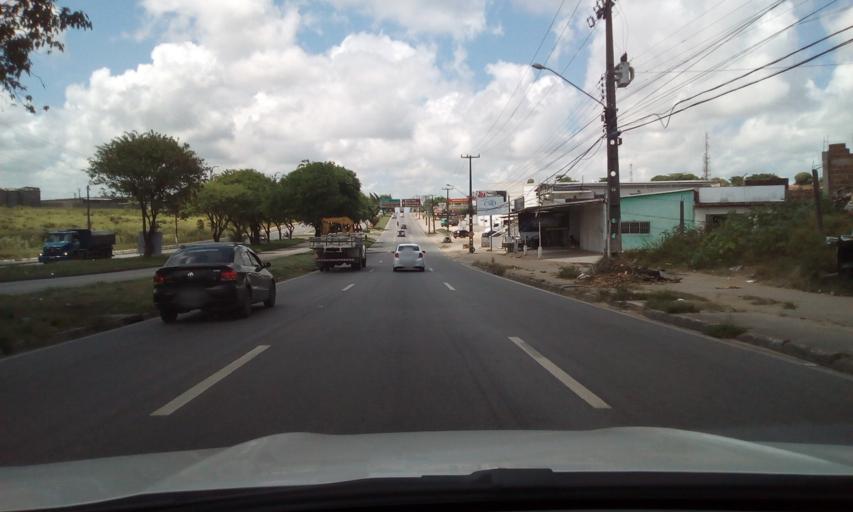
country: BR
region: Pernambuco
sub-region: Igarassu
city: Igarassu
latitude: -7.8461
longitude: -34.9101
